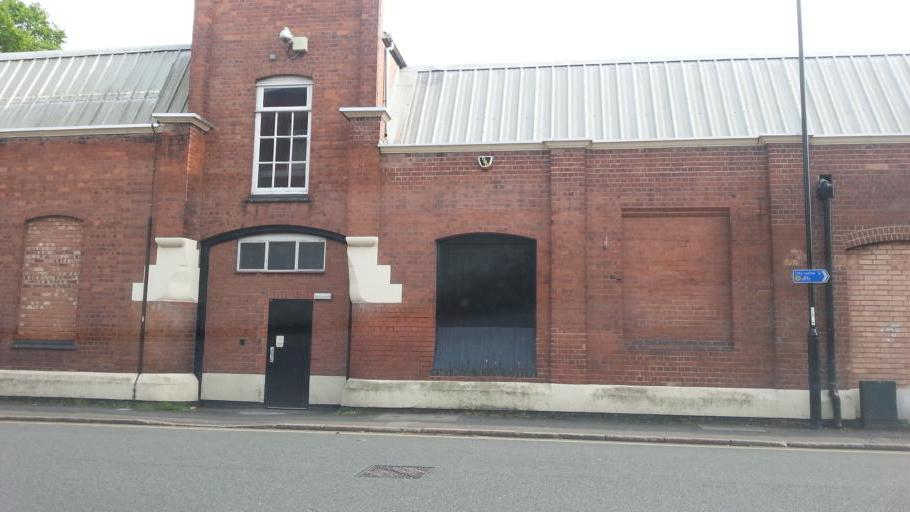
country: GB
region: England
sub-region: Coventry
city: Coventry
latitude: 52.4103
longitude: -1.4996
